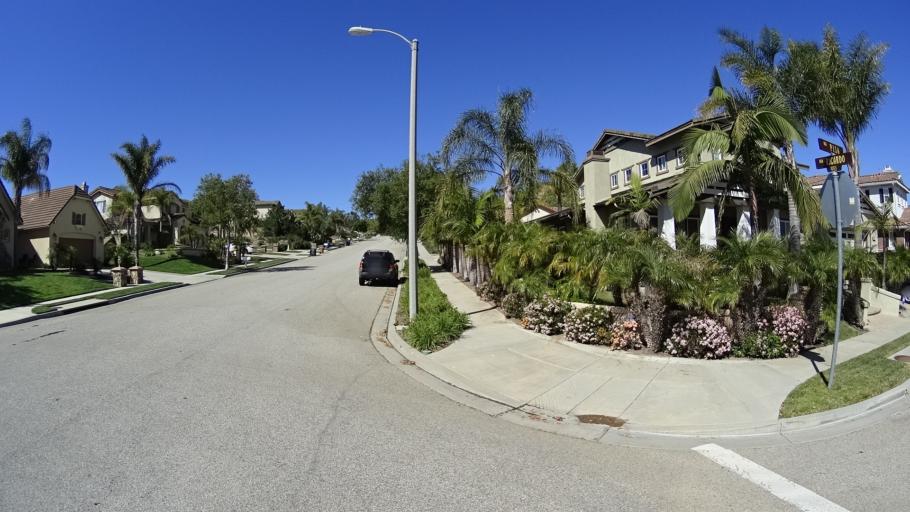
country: US
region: California
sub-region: Ventura County
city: Casa Conejo
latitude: 34.1776
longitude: -118.9875
